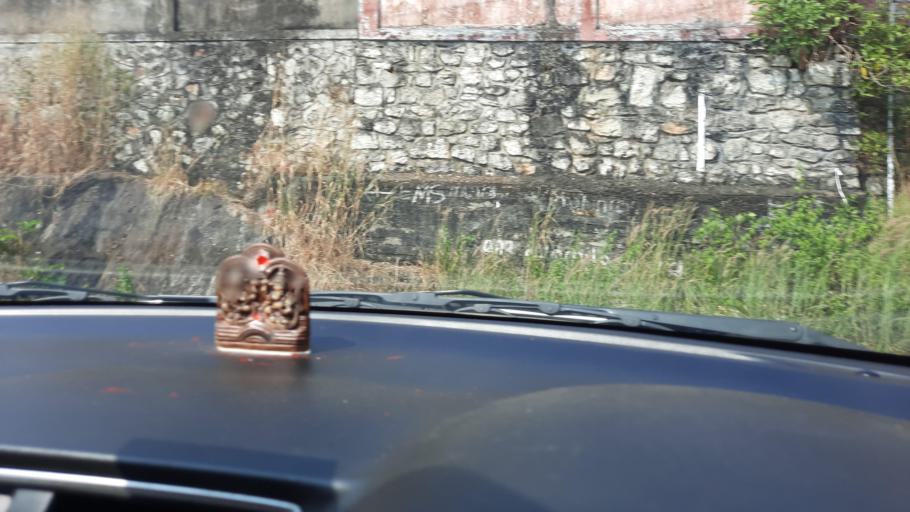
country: IN
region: Kerala
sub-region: Thiruvananthapuram
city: Nedumangad
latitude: 8.5898
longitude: 76.9296
